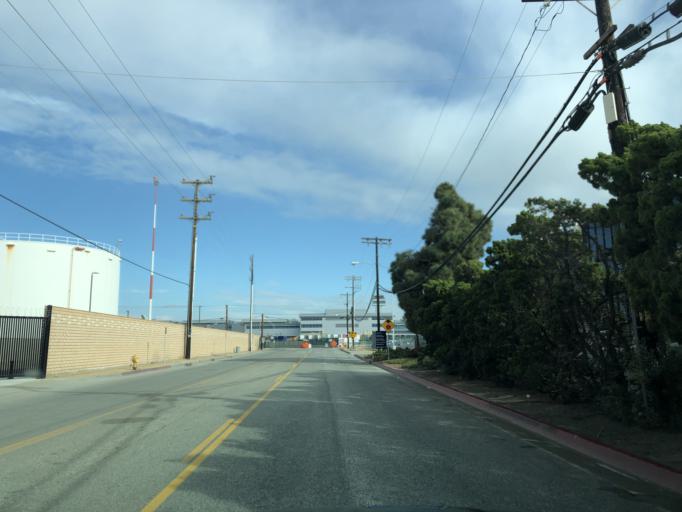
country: US
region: California
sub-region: Los Angeles County
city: El Segundo
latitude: 33.9419
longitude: -118.4210
